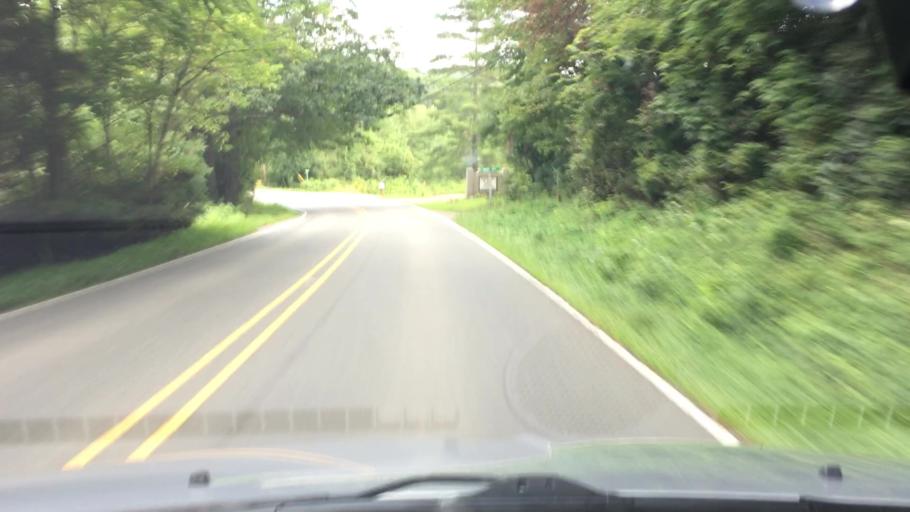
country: US
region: North Carolina
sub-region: Yancey County
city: Burnsville
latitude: 35.8432
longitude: -82.1899
